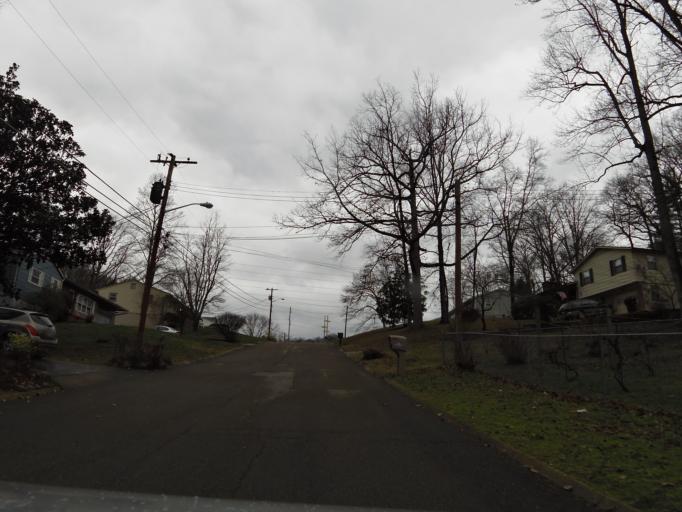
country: US
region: Tennessee
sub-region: Knox County
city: Knoxville
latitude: 35.9867
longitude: -84.0197
